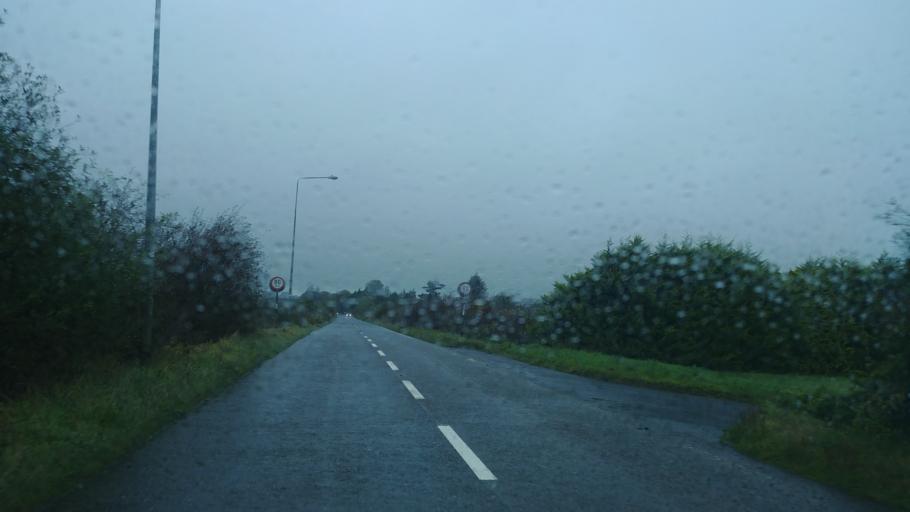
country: IE
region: Connaught
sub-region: Roscommon
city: Ballaghaderreen
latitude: 53.9077
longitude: -8.5917
